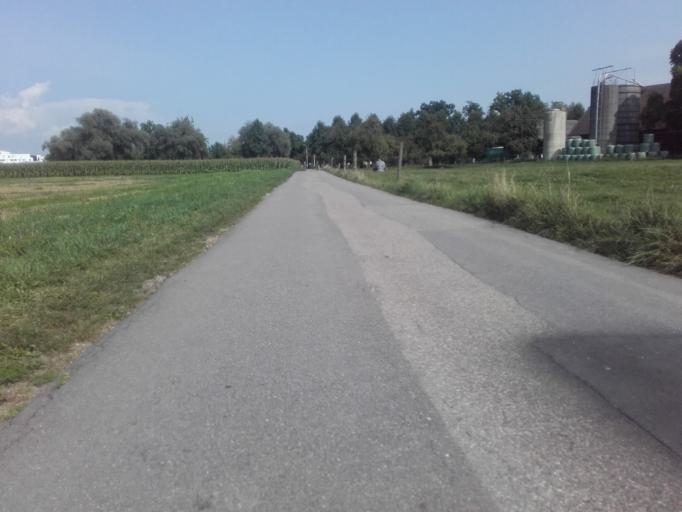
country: CH
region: Solothurn
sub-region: Bezirk Solothurn
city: Solothurn
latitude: 47.1990
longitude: 7.5207
